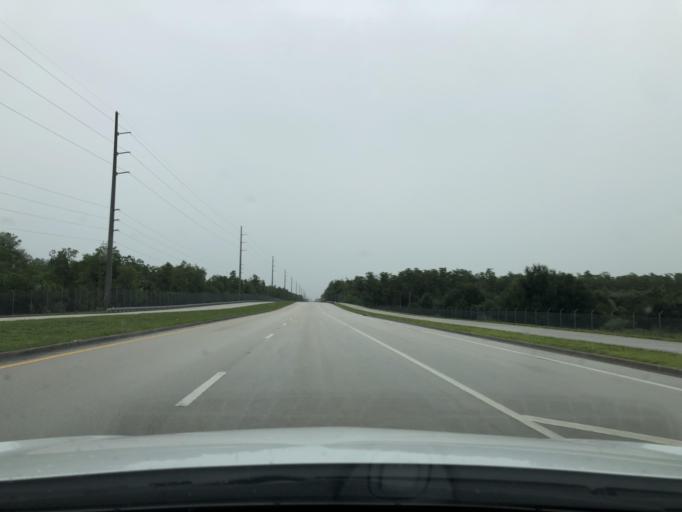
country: US
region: Florida
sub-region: Collier County
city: Orangetree
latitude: 26.2943
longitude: -81.4660
